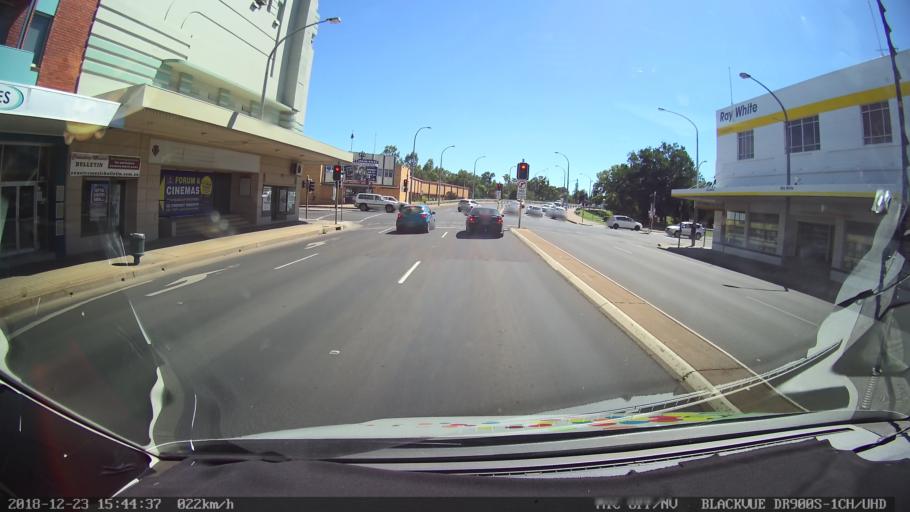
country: AU
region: New South Wales
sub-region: Tamworth Municipality
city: Tamworth
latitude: -31.0906
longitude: 150.9286
